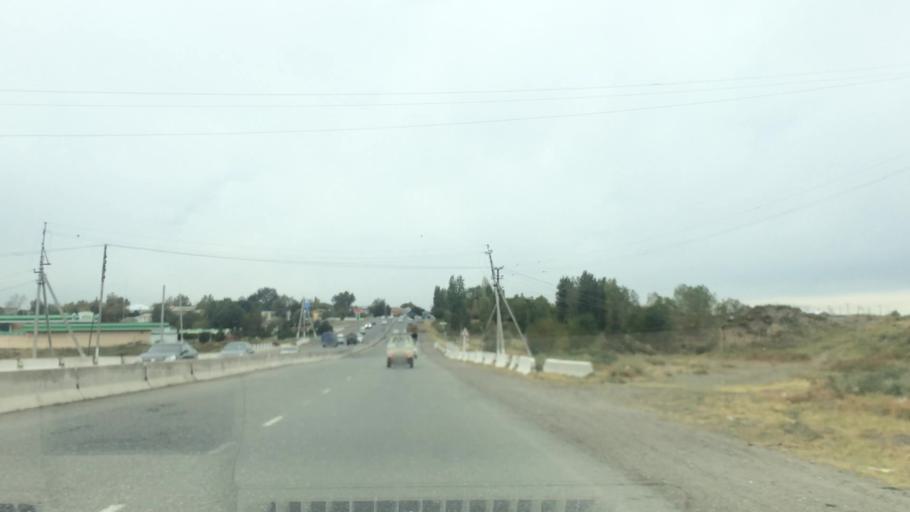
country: UZ
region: Samarqand
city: Bulung'ur
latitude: 39.7736
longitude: 67.2808
